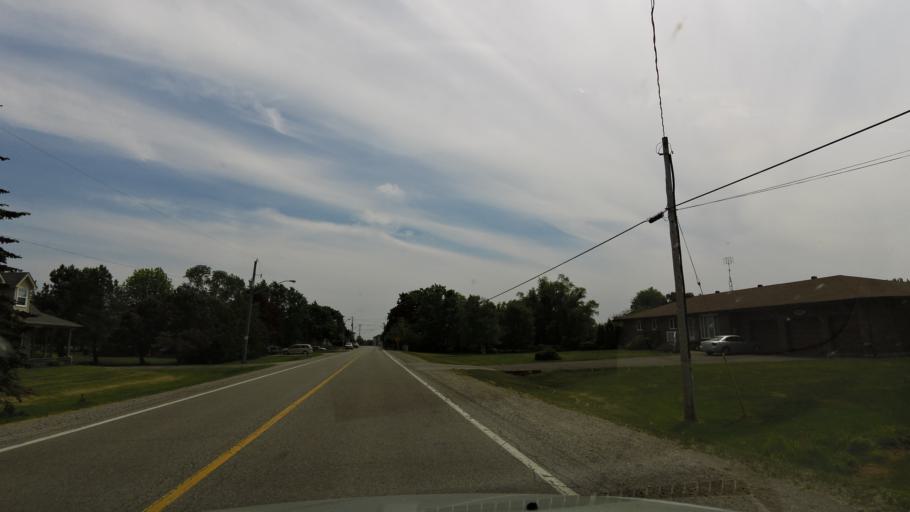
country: CA
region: Ontario
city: Cobourg
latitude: 43.9411
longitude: -78.4937
